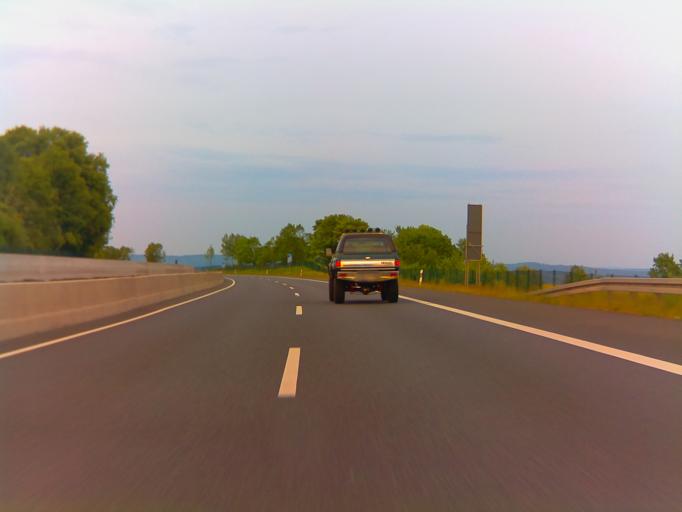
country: DE
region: Hesse
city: Gudensberg
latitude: 51.1877
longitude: 9.3867
